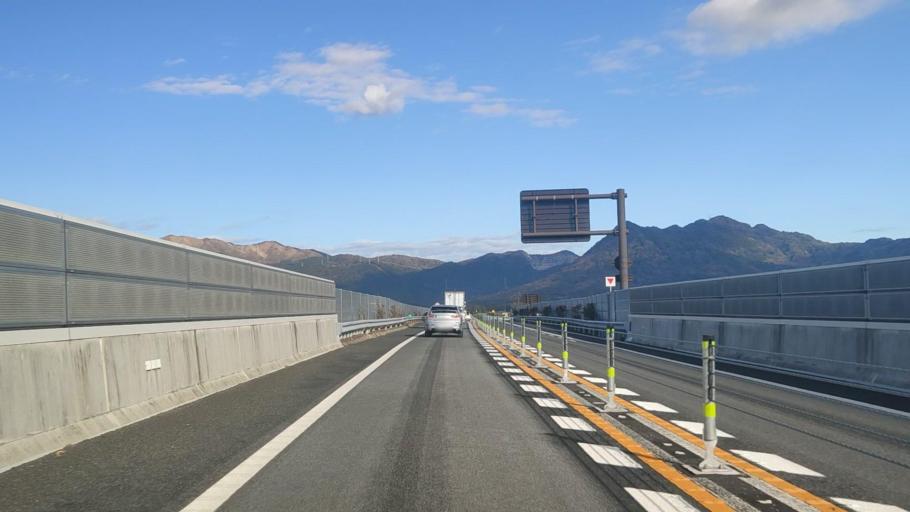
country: JP
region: Fukuoka
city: Yukuhashi
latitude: 33.7290
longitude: 130.9474
